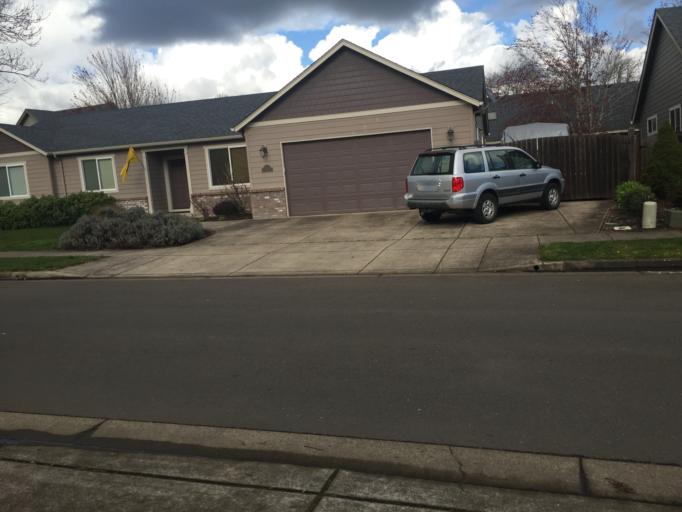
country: US
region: Oregon
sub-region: Lane County
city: Eugene
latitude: 44.1000
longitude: -123.1559
